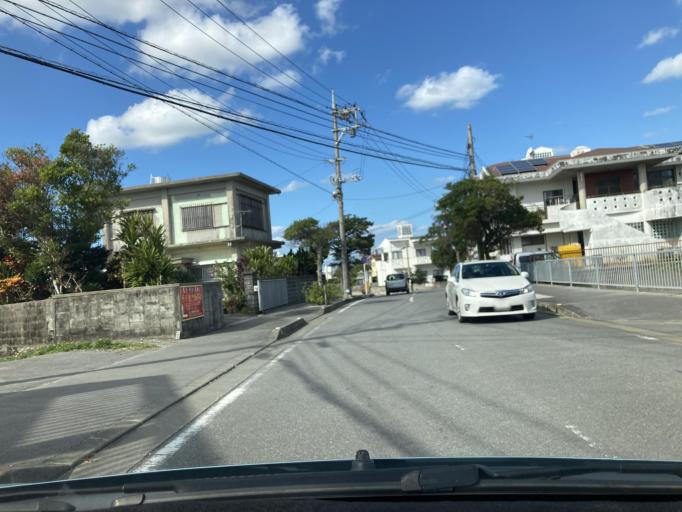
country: JP
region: Okinawa
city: Gushikawa
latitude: 26.3667
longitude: 127.8436
